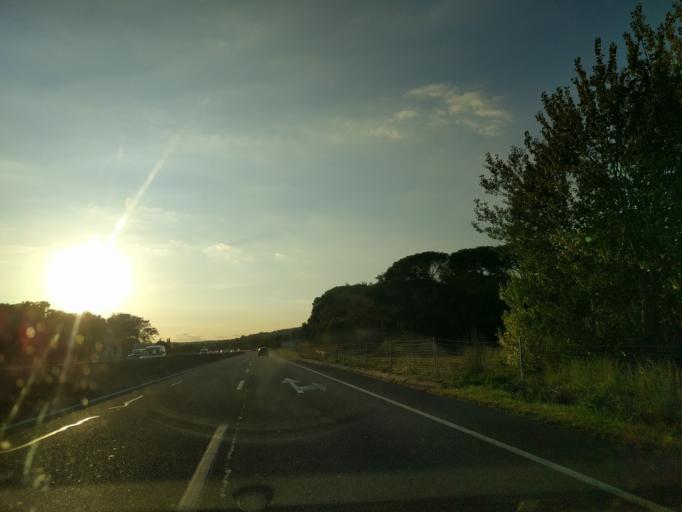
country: ES
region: Catalonia
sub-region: Provincia de Girona
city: Santa Cristina d'Aro
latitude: 41.8274
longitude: 2.9679
